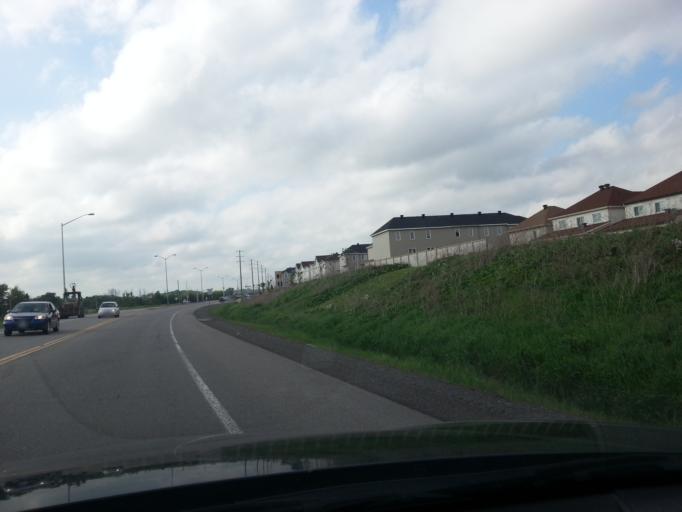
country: CA
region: Ontario
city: Bells Corners
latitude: 45.2621
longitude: -75.7757
